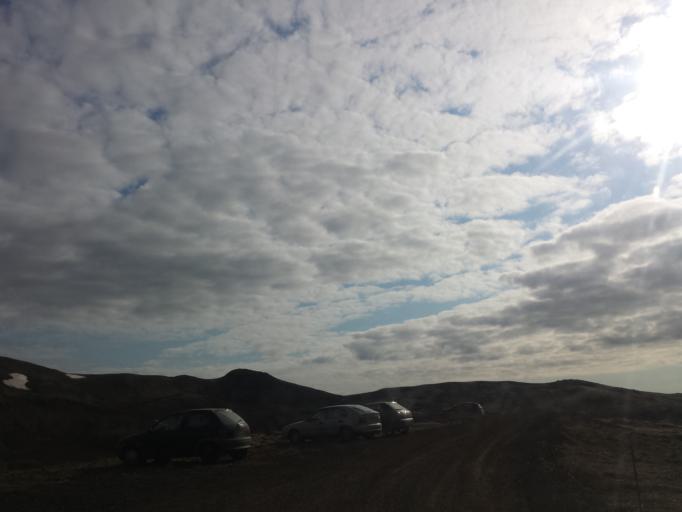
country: IS
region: Capital Region
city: Mosfellsbaer
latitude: 64.0707
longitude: -21.6583
